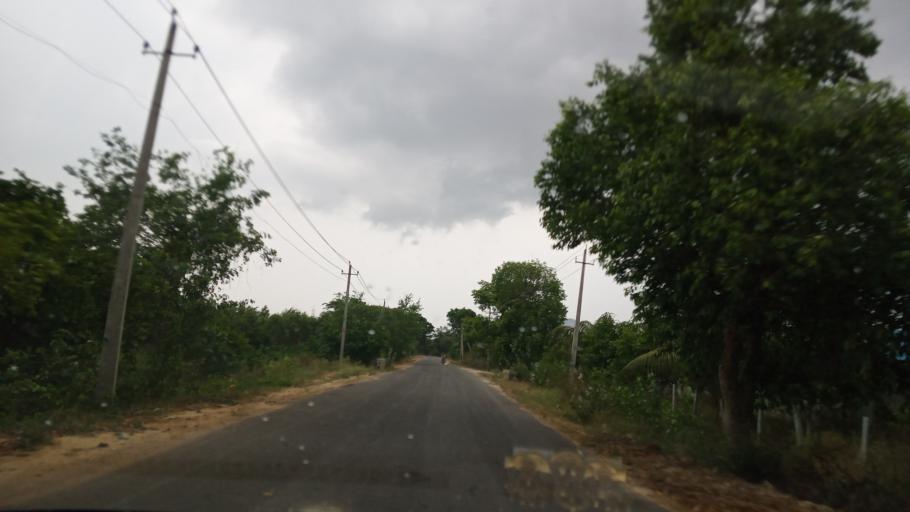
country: IN
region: Karnataka
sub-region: Kolar
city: Mulbagal
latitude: 13.1203
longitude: 78.3422
